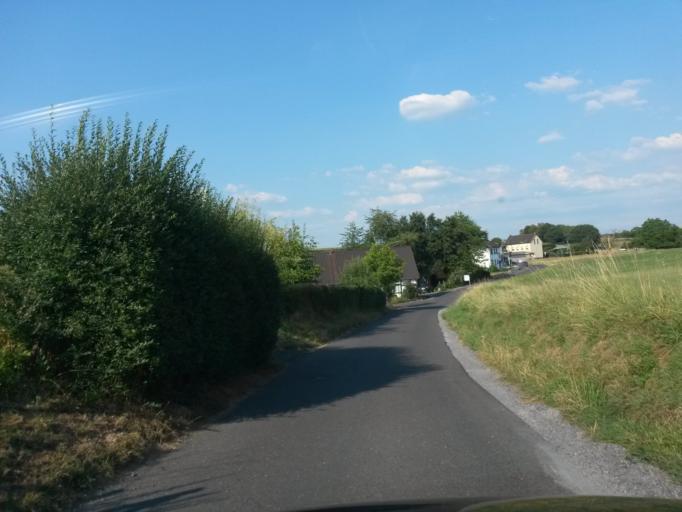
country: DE
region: North Rhine-Westphalia
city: Lohmar
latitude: 50.8820
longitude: 7.2247
